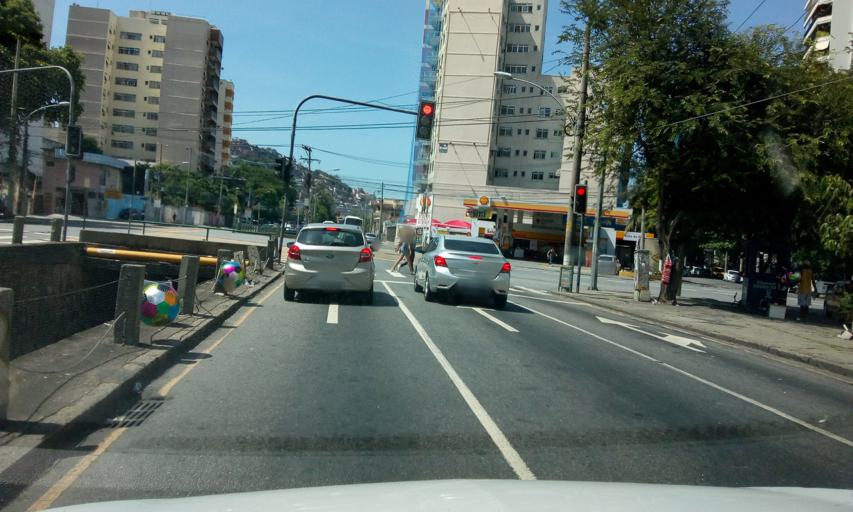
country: BR
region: Rio de Janeiro
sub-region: Rio De Janeiro
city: Rio de Janeiro
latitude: -22.9144
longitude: -43.2340
